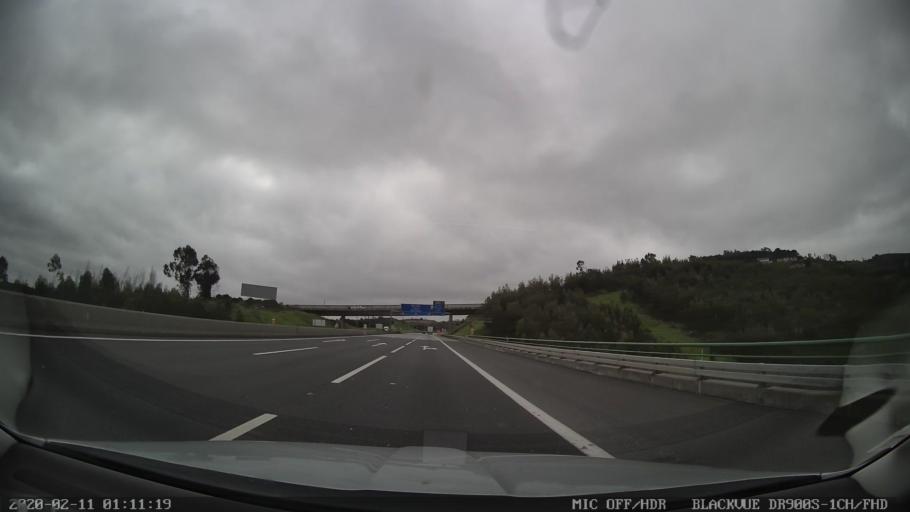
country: PT
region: Lisbon
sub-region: Loures
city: Loures
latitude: 38.8308
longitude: -9.1896
